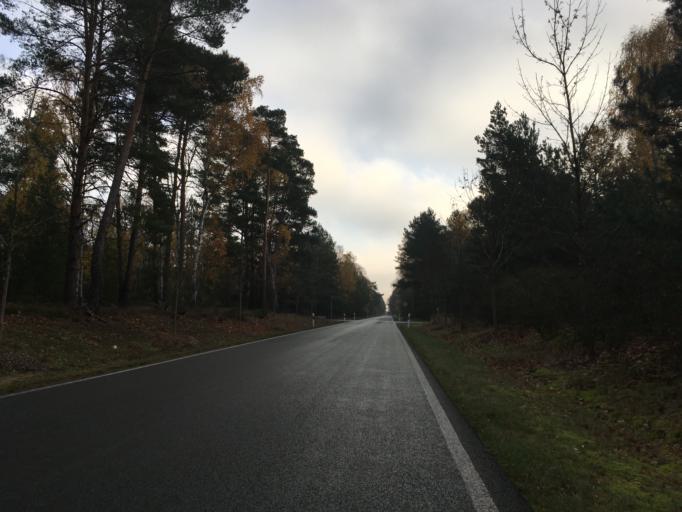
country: DE
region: Brandenburg
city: Halbe
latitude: 52.0325
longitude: 13.7671
